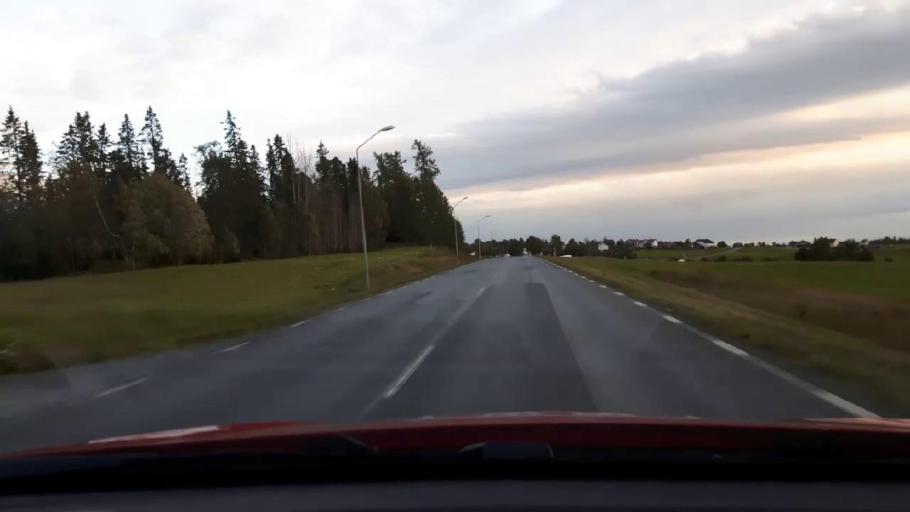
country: SE
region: Jaemtland
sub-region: OEstersunds Kommun
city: Ostersund
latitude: 63.1126
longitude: 14.4344
